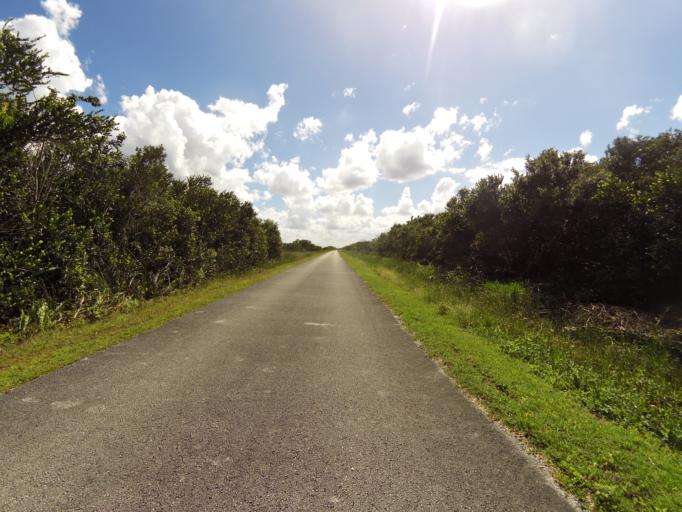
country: US
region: Florida
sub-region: Miami-Dade County
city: The Hammocks
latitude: 25.7088
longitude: -80.7668
